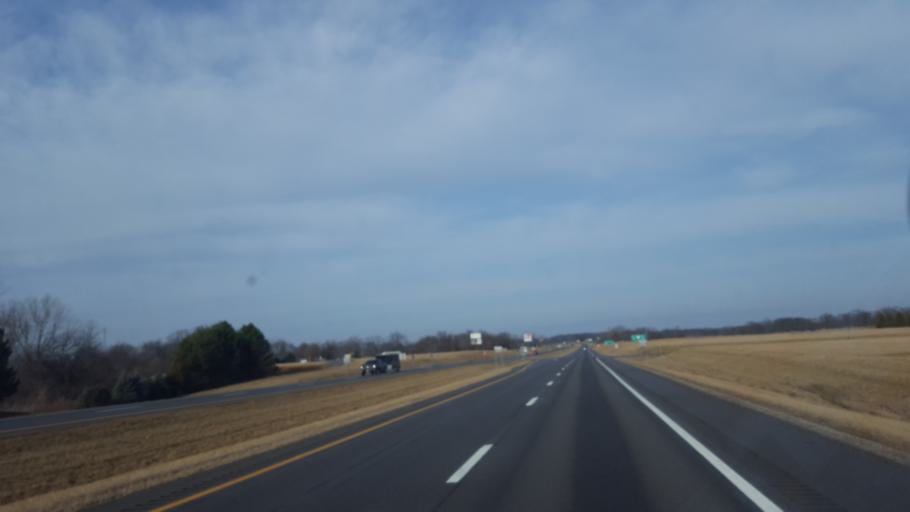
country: US
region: Ohio
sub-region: Wyandot County
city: Upper Sandusky
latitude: 40.7372
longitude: -83.2075
